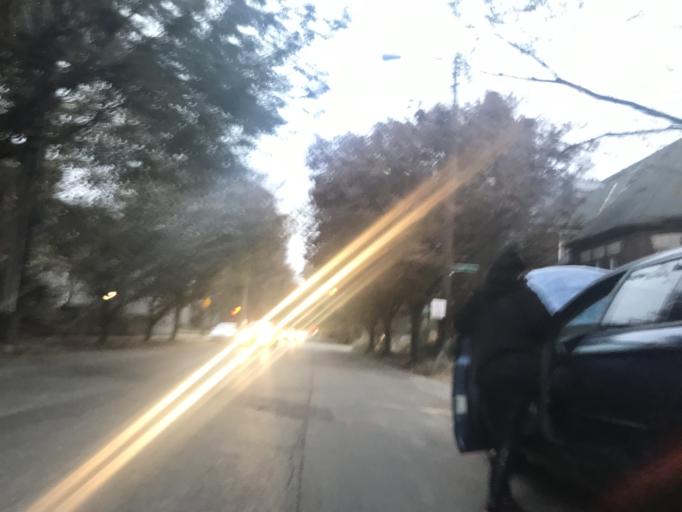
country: US
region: Kentucky
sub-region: Jefferson County
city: Louisville
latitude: 38.2290
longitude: -85.7647
